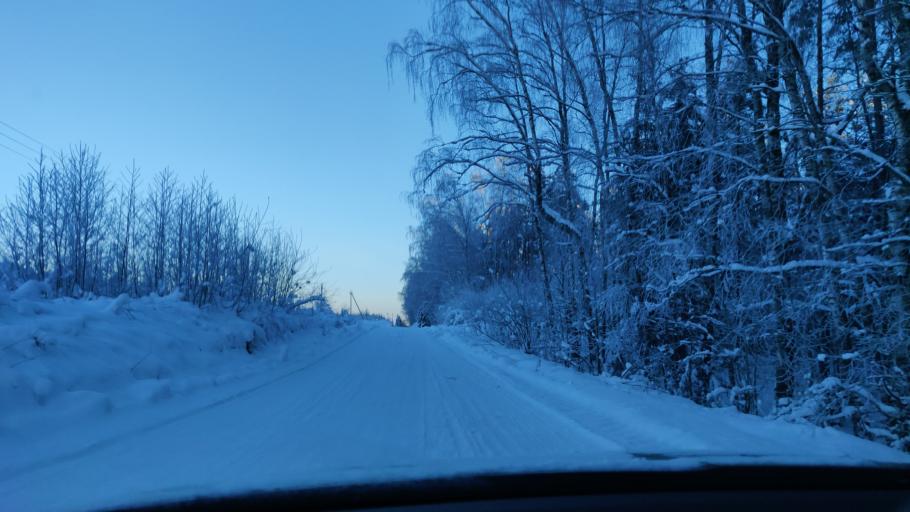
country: LT
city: Trakai
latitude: 54.6150
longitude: 24.9490
